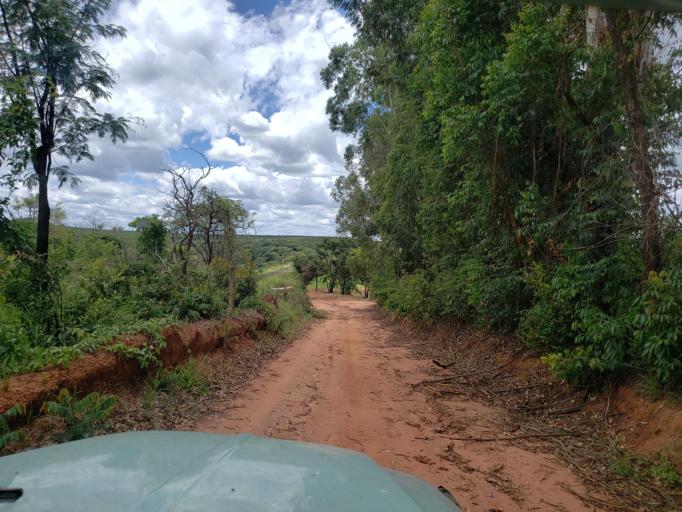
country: BR
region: Sao Paulo
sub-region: Aguai
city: Aguai
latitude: -22.1877
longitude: -46.9496
